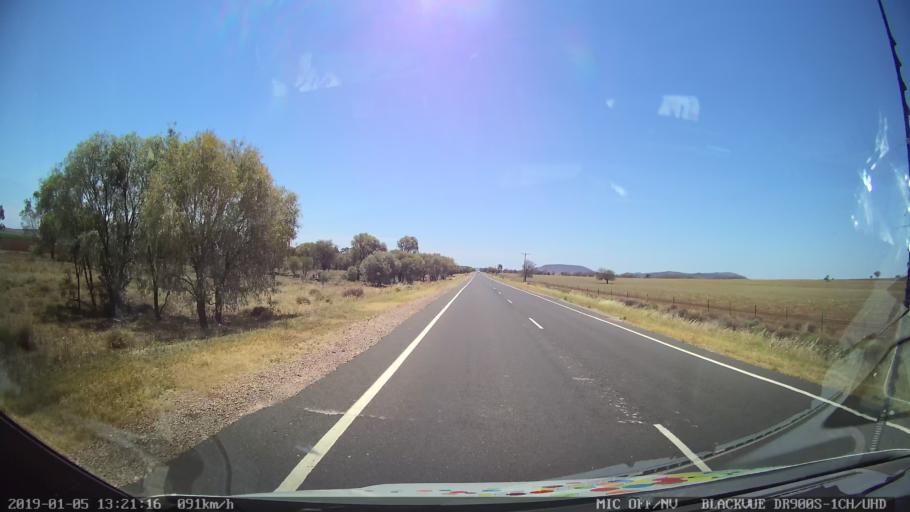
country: AU
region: New South Wales
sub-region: Gunnedah
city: Gunnedah
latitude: -31.0957
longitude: 149.9465
